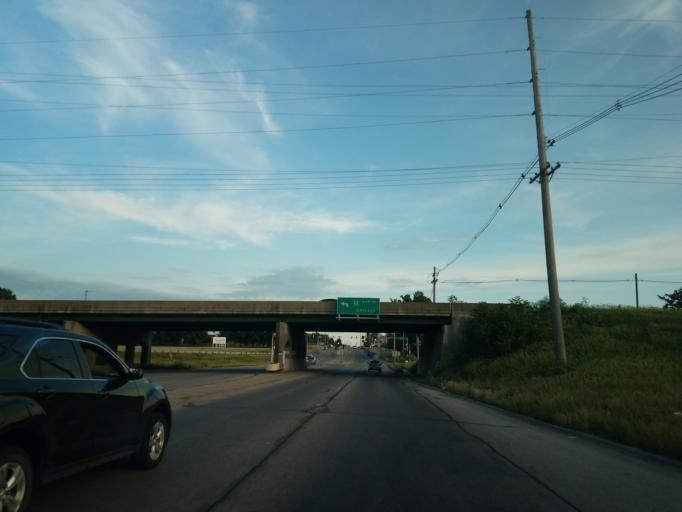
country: US
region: Illinois
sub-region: McLean County
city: Bloomington
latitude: 40.4597
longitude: -88.9930
